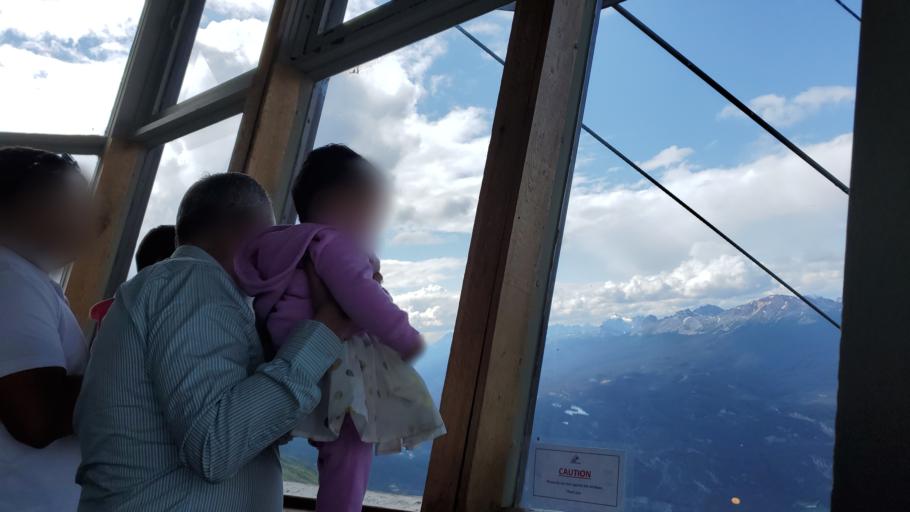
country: CA
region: Alberta
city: Jasper Park Lodge
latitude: 52.8359
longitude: -118.1265
